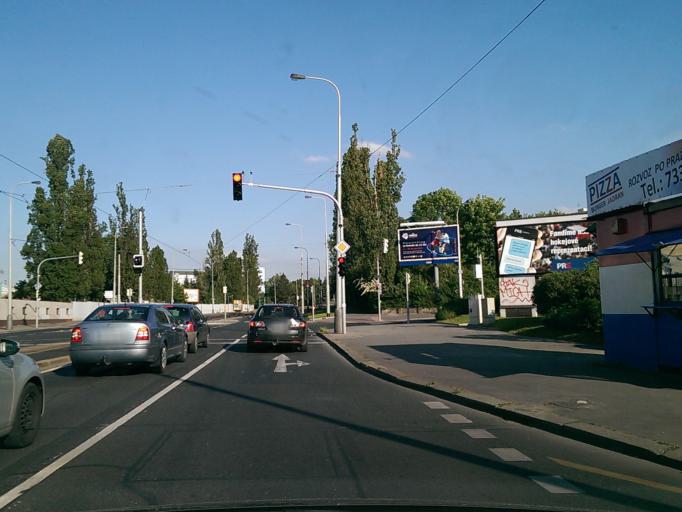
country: CZ
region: Praha
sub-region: Praha 9
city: Vysocany
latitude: 50.0603
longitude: 14.5066
